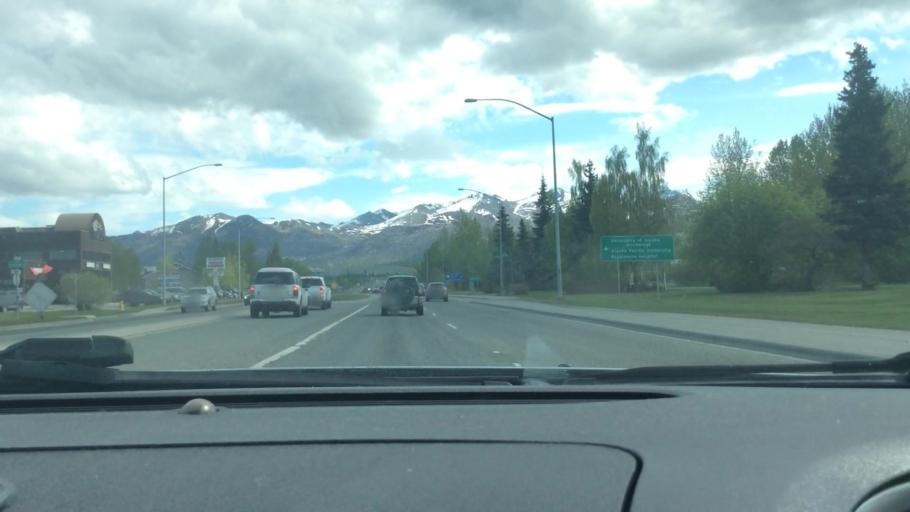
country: US
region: Alaska
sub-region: Anchorage Municipality
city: Anchorage
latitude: 61.1808
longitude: -149.8142
